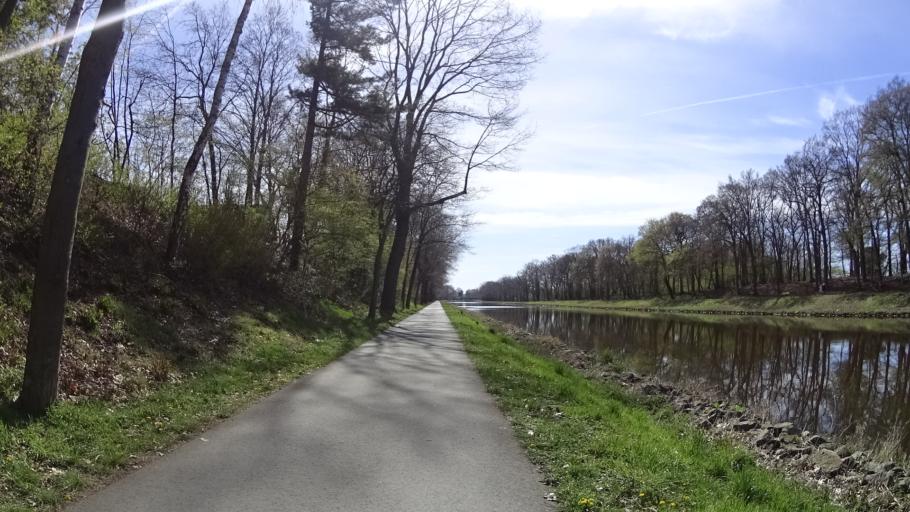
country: DE
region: Lower Saxony
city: Lingen
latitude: 52.5338
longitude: 7.3018
